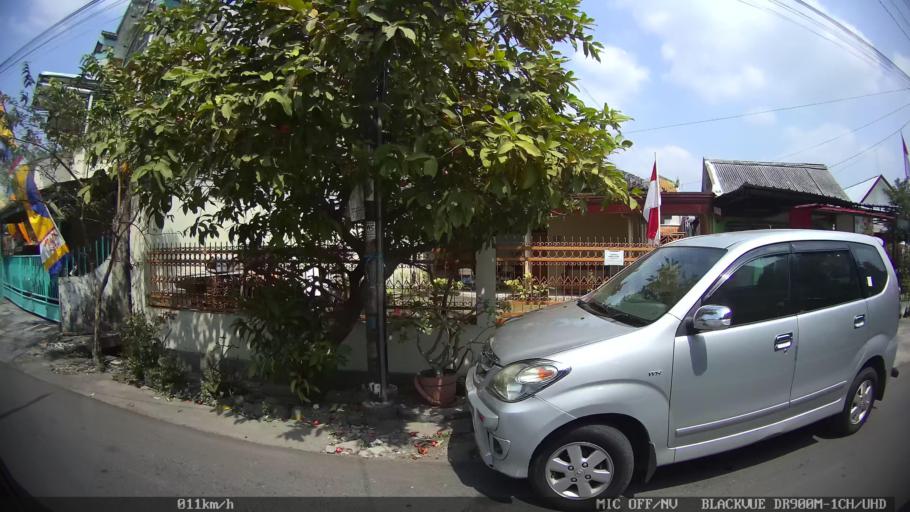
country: ID
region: Daerah Istimewa Yogyakarta
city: Yogyakarta
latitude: -7.8058
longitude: 110.3871
